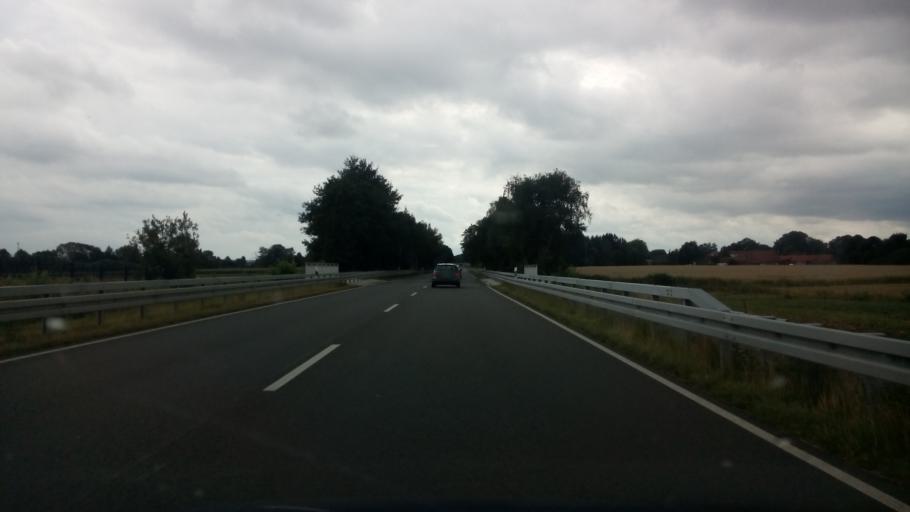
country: DE
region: Lower Saxony
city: Lembruch
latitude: 52.5278
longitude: 8.3761
